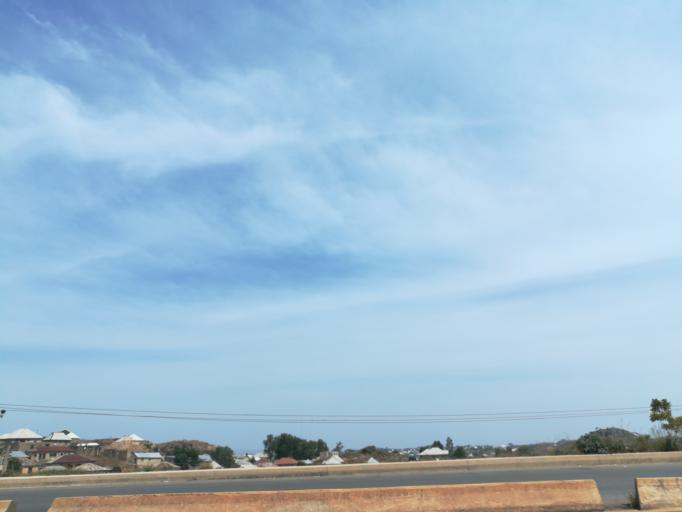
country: NG
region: Plateau
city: Bukuru
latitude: 9.8342
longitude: 8.8670
